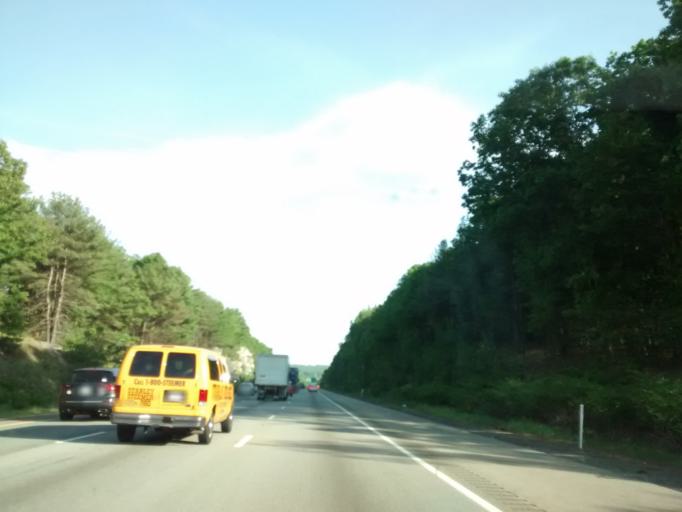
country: US
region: Massachusetts
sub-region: Worcester County
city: Berlin
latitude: 42.3826
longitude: -71.6024
